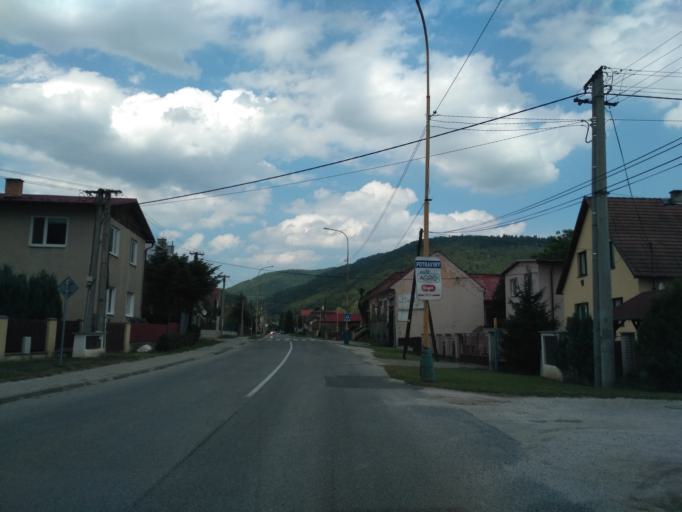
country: SK
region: Kosicky
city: Gelnica
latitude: 48.8909
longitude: 21.0117
